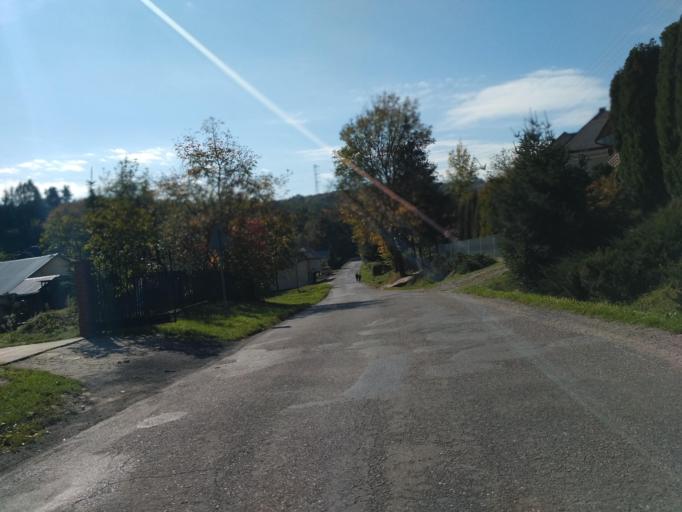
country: PL
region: Subcarpathian Voivodeship
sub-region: Powiat debicki
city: Slotowa
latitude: 49.9429
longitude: 21.2850
